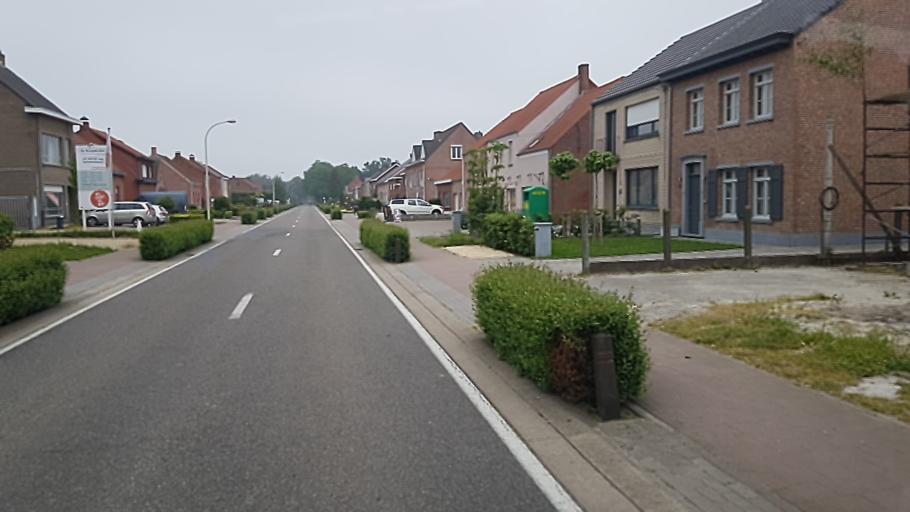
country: BE
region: Flanders
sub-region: Provincie Antwerpen
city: Brecht
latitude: 51.3330
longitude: 4.6697
